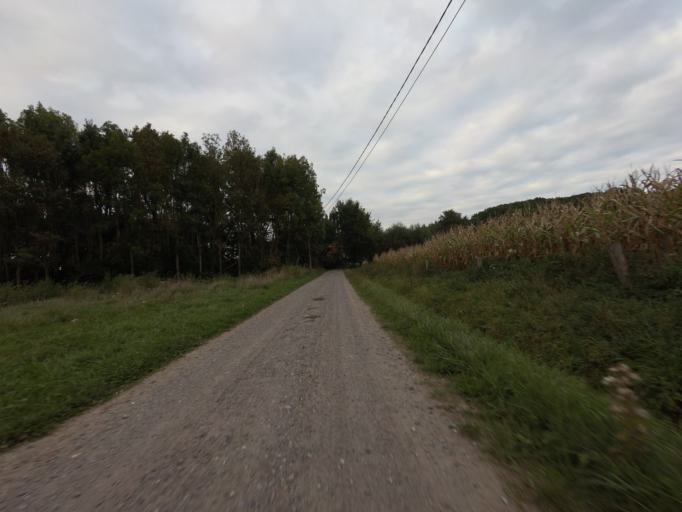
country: BE
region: Flanders
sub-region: Provincie Vlaams-Brabant
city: Boortmeerbeek
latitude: 50.9581
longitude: 4.5742
